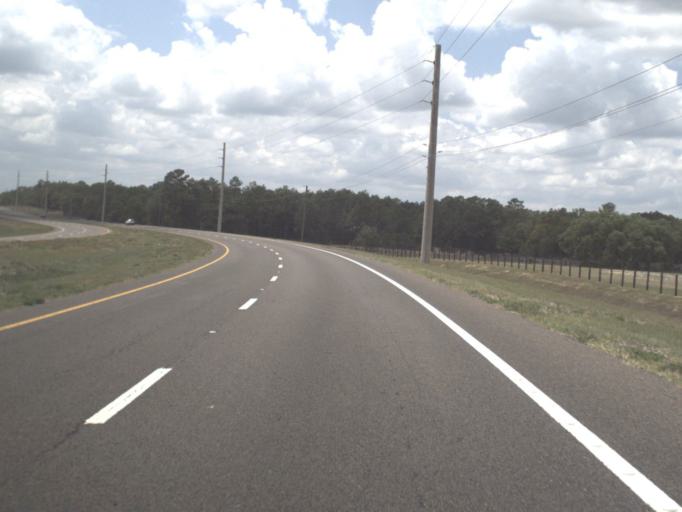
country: US
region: Florida
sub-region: Sumter County
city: Wildwood
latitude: 28.8803
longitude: -82.1249
